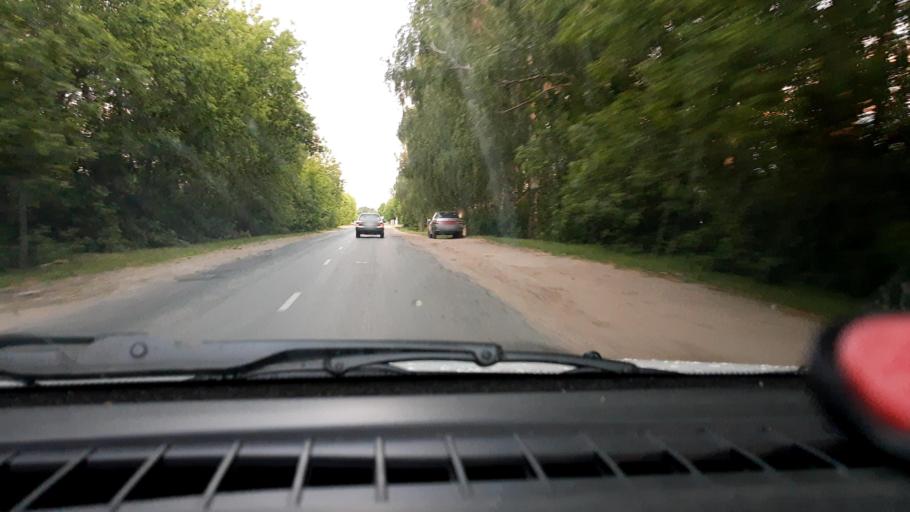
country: RU
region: Nizjnij Novgorod
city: Kstovo
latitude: 56.1325
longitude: 44.0864
